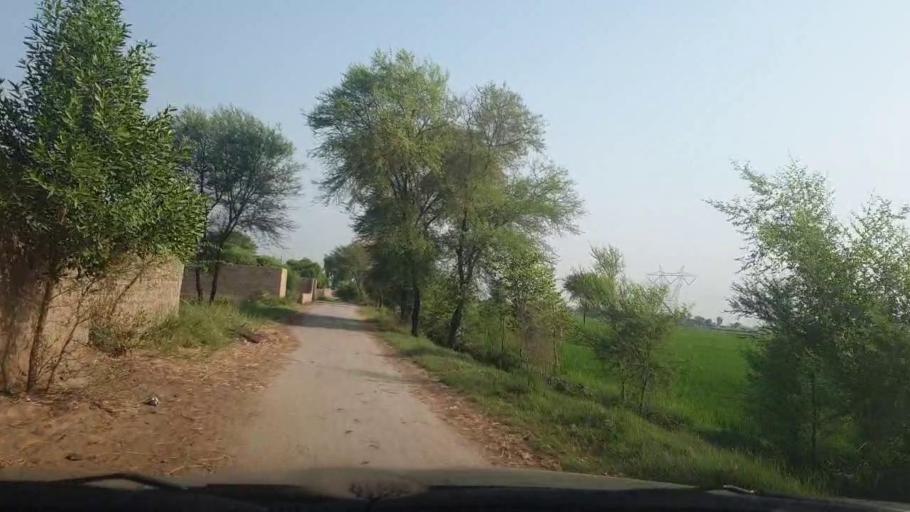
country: PK
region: Sindh
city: Larkana
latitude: 27.5896
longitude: 68.1607
